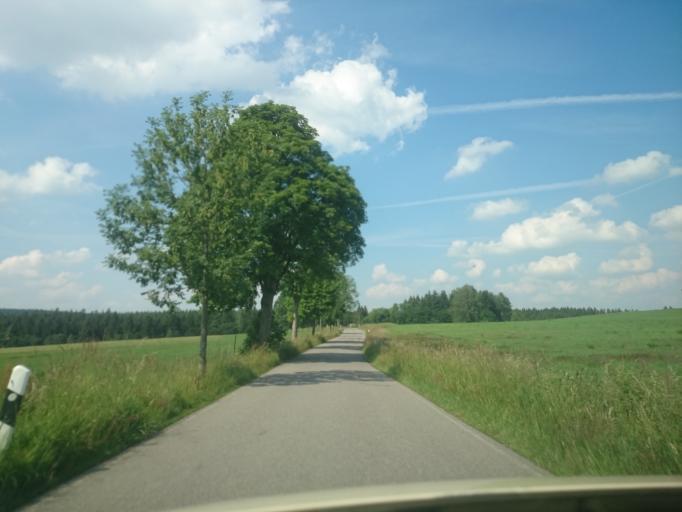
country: DE
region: Saxony
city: Lengefeld
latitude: 50.7475
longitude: 13.2134
